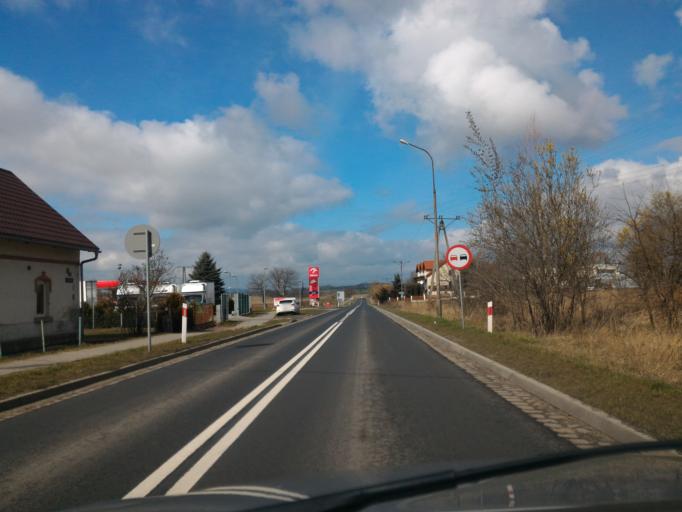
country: PL
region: Silesian Voivodeship
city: Zawidow
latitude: 51.0318
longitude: 15.0552
